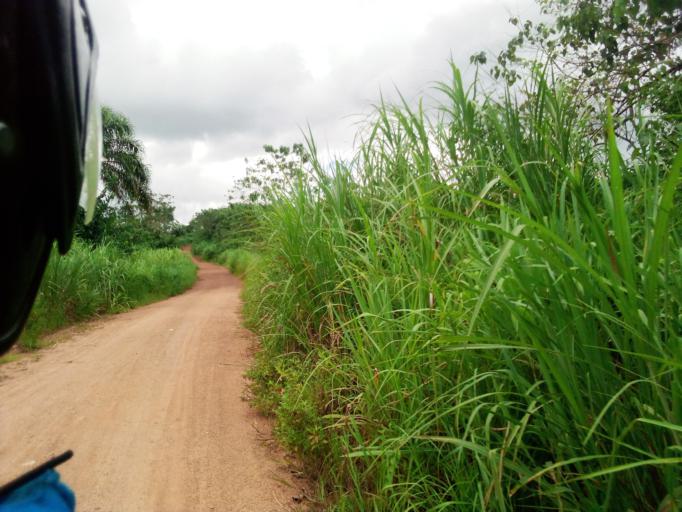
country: SL
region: Eastern Province
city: Simbakoro
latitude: 8.5919
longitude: -10.9856
